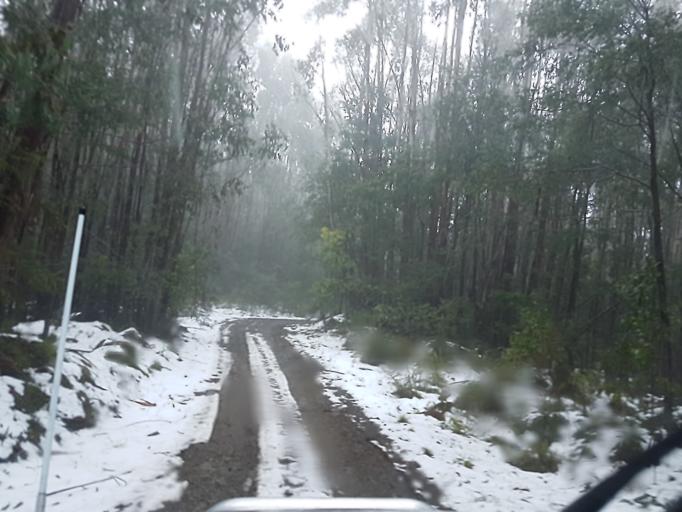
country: AU
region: Victoria
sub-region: Yarra Ranges
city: Millgrove
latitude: -37.5423
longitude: 145.8955
